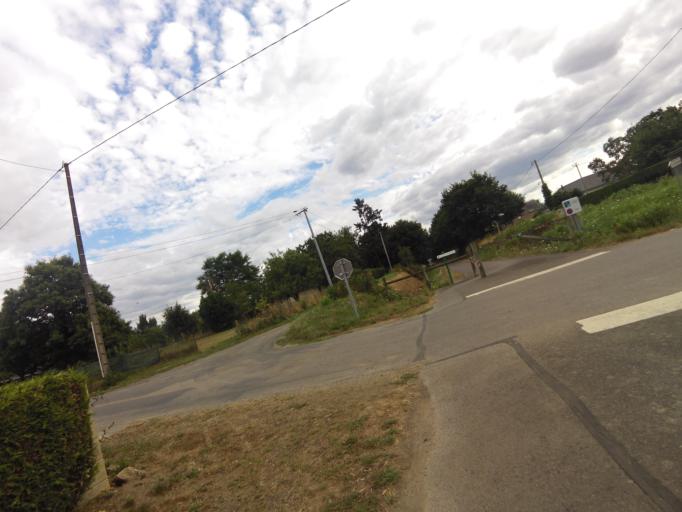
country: FR
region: Brittany
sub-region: Departement du Morbihan
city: Guillac
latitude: 47.8585
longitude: -2.4395
